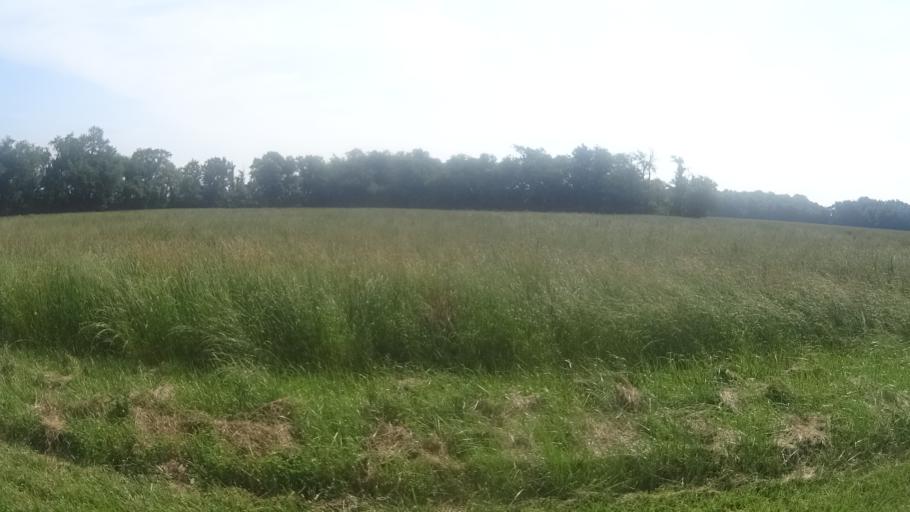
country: US
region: Ohio
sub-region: Huron County
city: Monroeville
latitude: 41.3047
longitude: -82.7121
